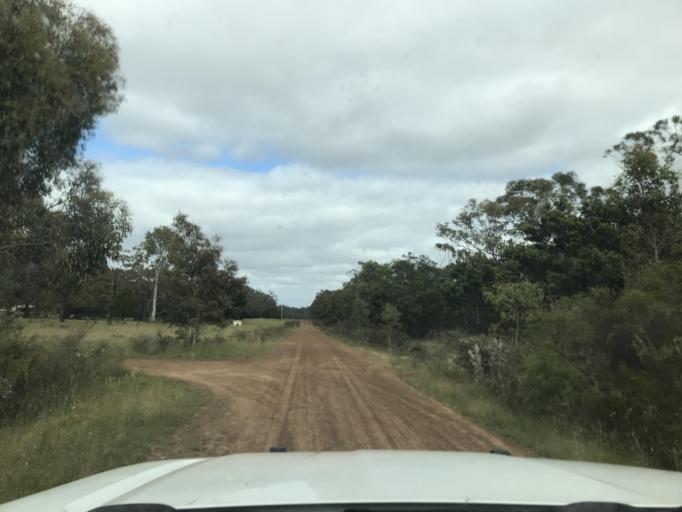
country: AU
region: South Australia
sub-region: Wattle Range
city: Penola
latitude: -37.3344
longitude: 141.4183
